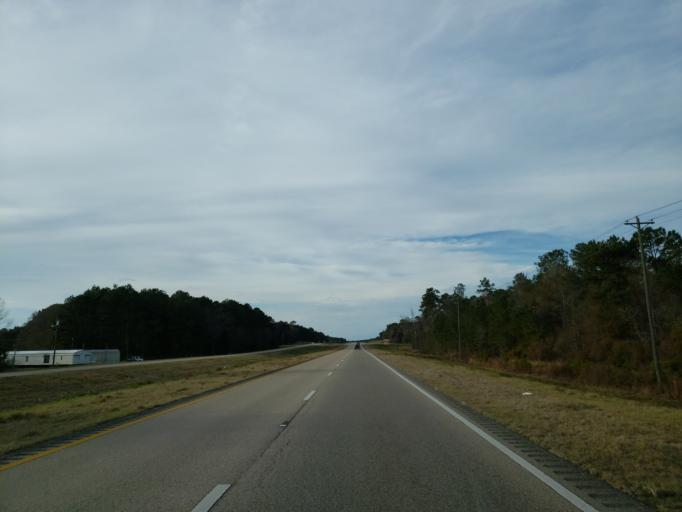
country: US
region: Mississippi
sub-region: Wayne County
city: Waynesboro
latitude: 31.6159
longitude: -88.5748
